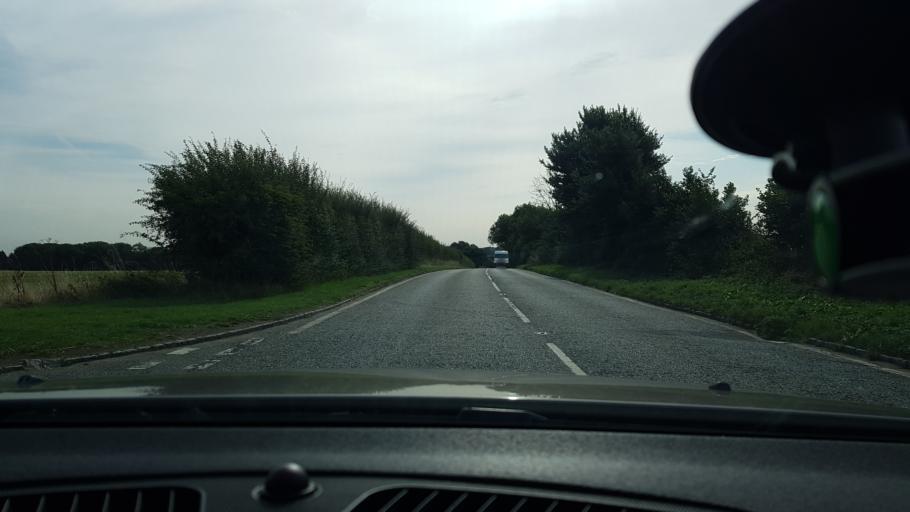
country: GB
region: England
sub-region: West Berkshire
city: Wickham
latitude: 51.4519
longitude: -1.4604
